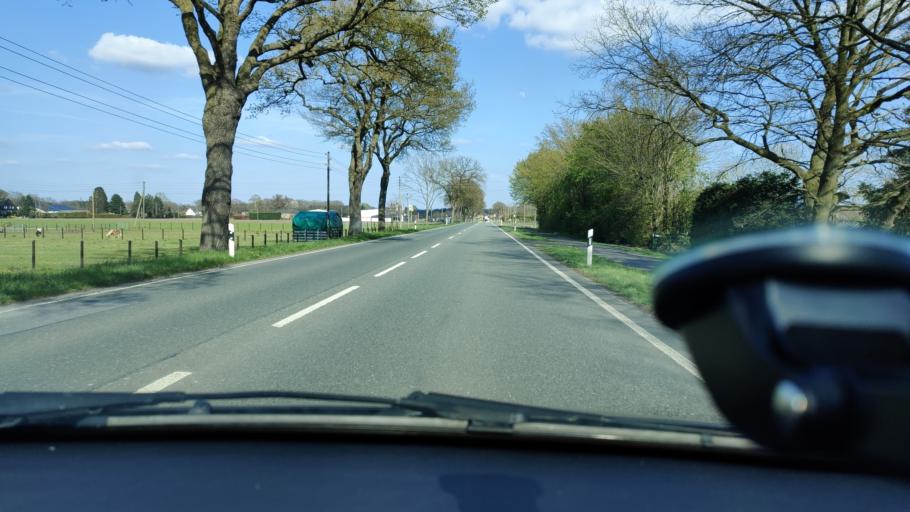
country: DE
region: North Rhine-Westphalia
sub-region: Regierungsbezirk Dusseldorf
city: Hunxe
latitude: 51.6678
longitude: 6.7256
